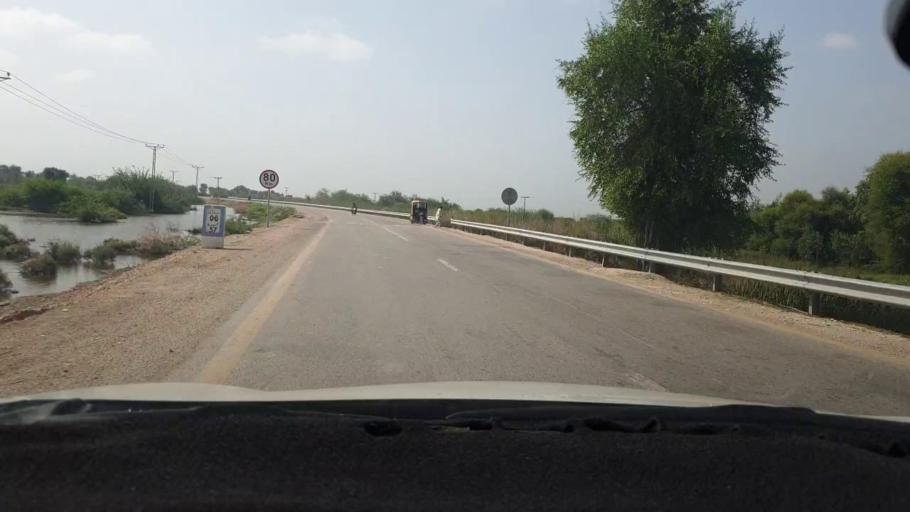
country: PK
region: Sindh
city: Mirpur Khas
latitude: 25.7499
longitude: 69.0844
